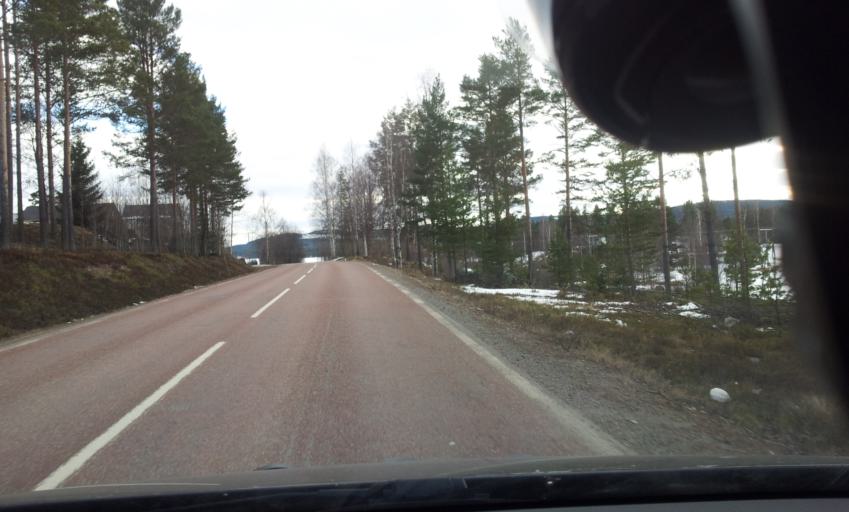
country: SE
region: Vaesternorrland
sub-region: Ange Kommun
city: Ange
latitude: 62.1572
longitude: 15.6769
